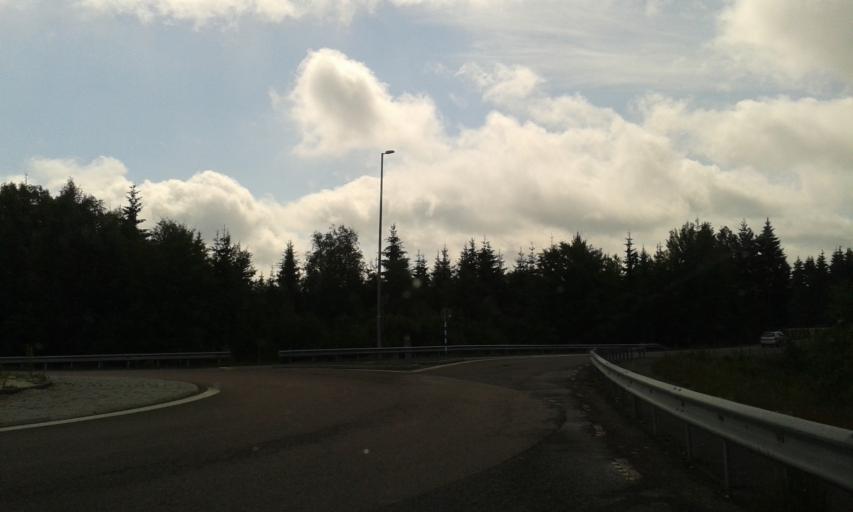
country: SE
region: Vaestra Goetaland
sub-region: Tranemo Kommun
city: Langhem
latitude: 57.6089
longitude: 13.1389
